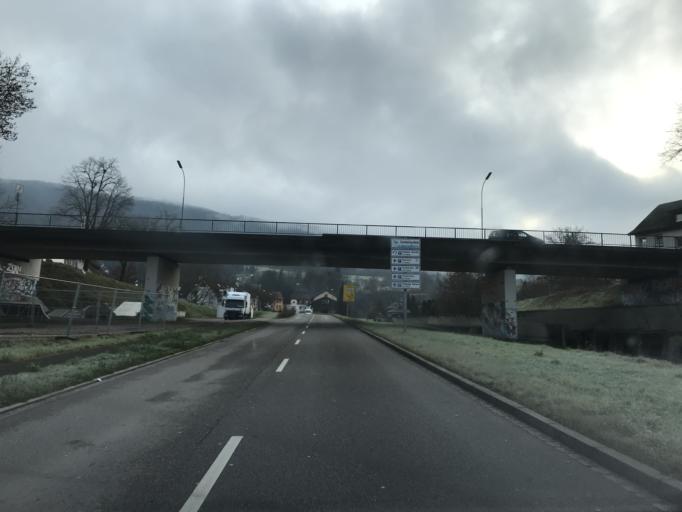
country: DE
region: Baden-Wuerttemberg
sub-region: Freiburg Region
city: Wehr
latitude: 47.6251
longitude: 7.9008
